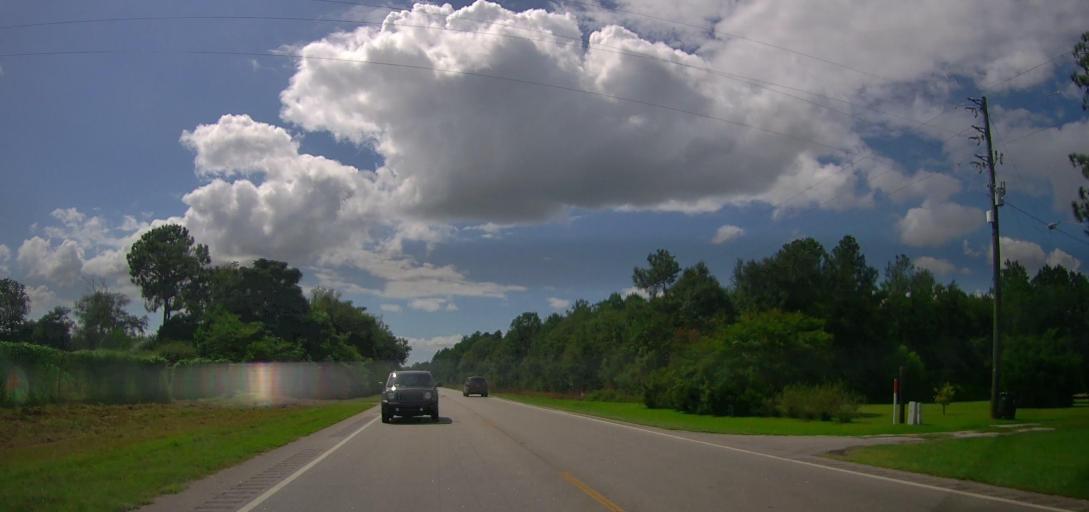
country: US
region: Georgia
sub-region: Coffee County
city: Broxton
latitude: 31.5571
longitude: -82.9698
